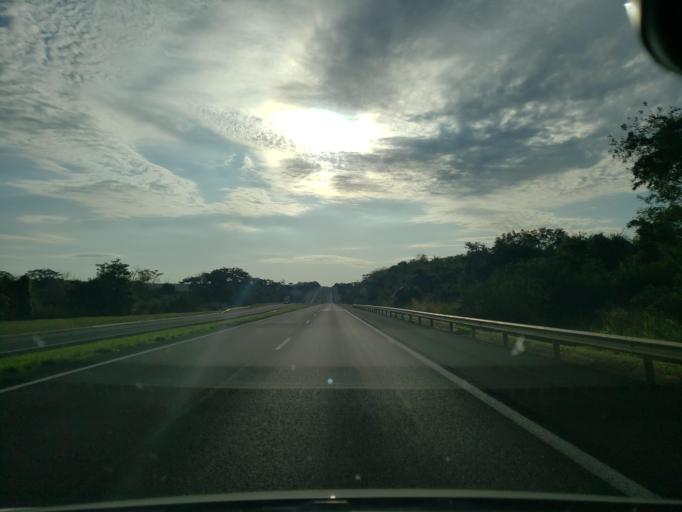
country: BR
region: Sao Paulo
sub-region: Mirandopolis
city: Mirandopolis
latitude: -21.1021
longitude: -51.0377
